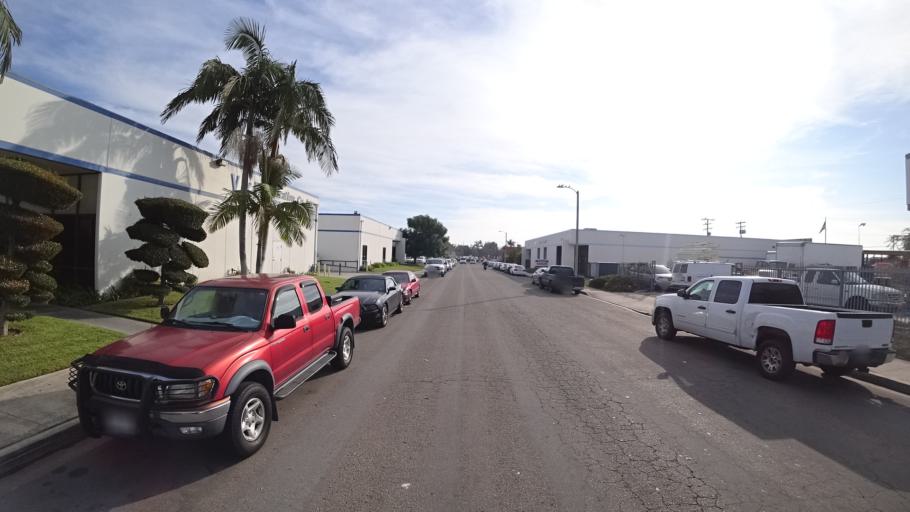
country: US
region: California
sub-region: Orange County
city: Garden Grove
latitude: 33.7611
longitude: -117.9226
